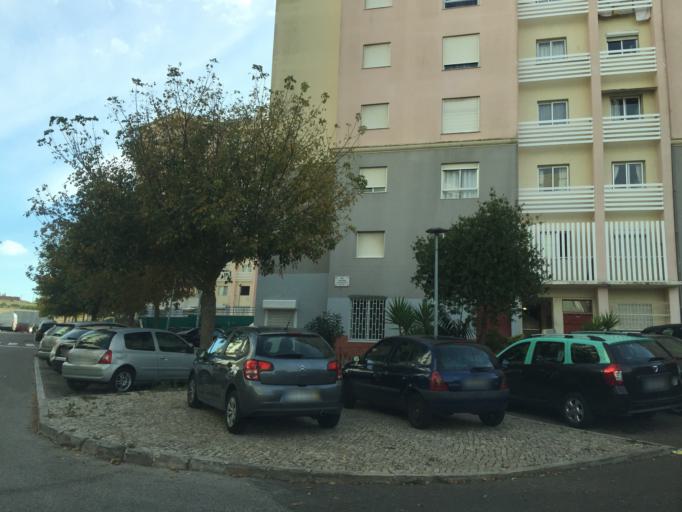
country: PT
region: Lisbon
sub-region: Odivelas
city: Olival do Basto
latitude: 38.7810
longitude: -9.1490
